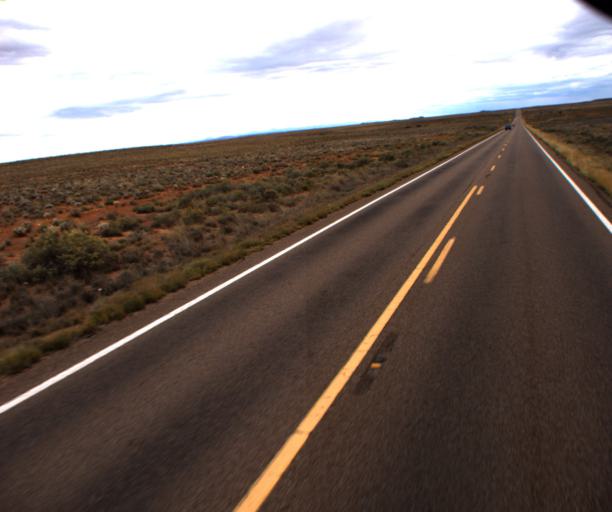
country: US
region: Arizona
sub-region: Navajo County
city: Holbrook
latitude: 34.7815
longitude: -110.1303
